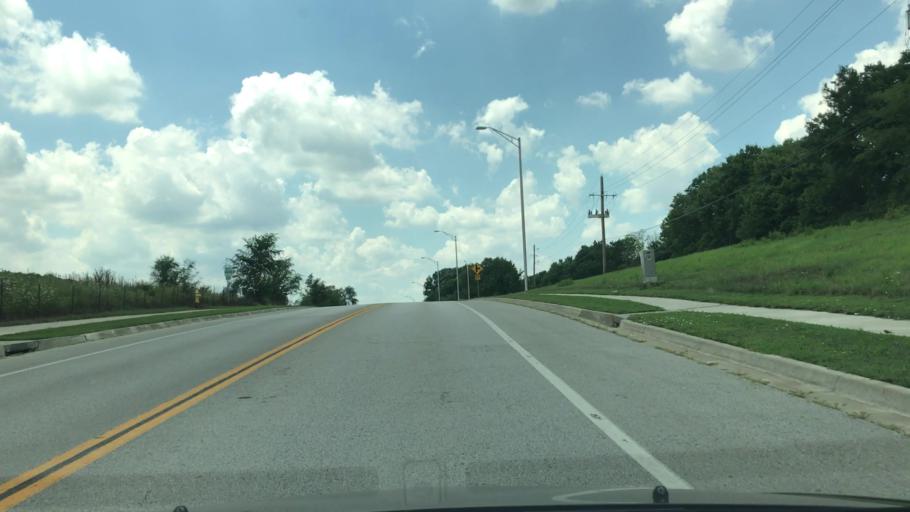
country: US
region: Missouri
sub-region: Jackson County
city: Lees Summit
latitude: 38.9047
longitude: -94.4172
